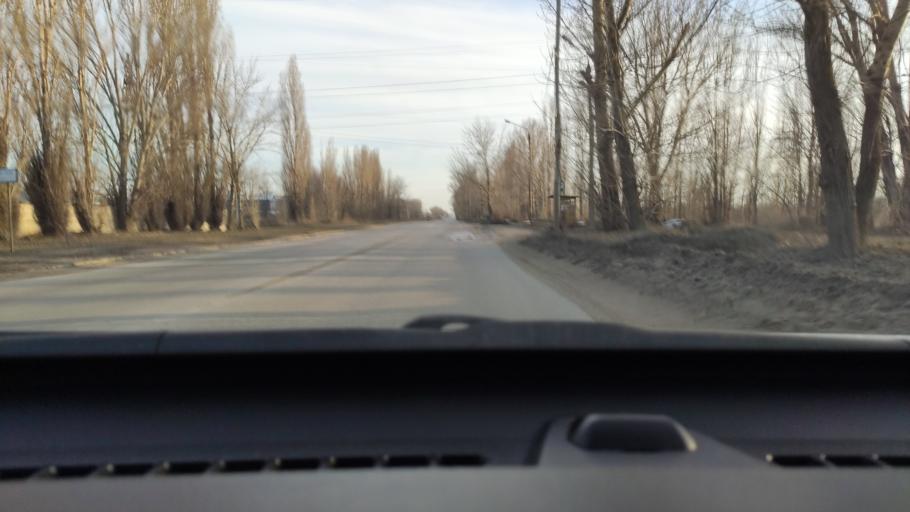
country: RU
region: Samara
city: Podstepki
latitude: 53.5837
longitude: 49.2231
